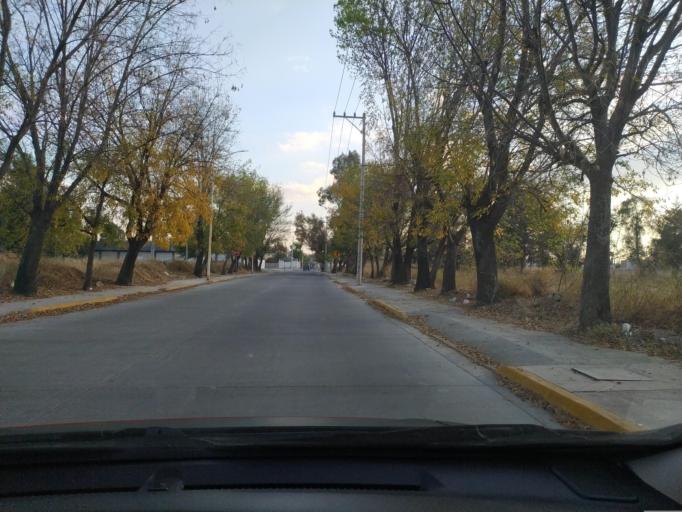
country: MX
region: Guanajuato
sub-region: San Francisco del Rincon
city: Estacion de San Francisco
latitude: 21.0281
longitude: -101.8299
